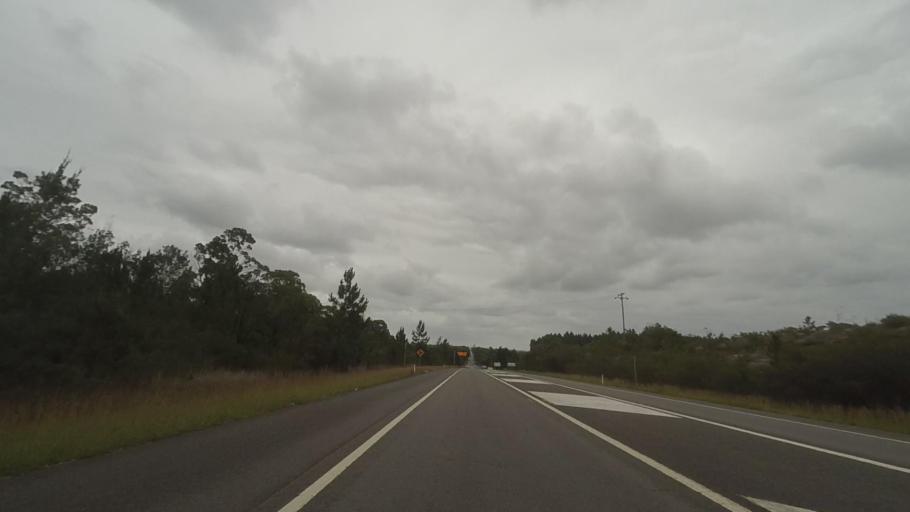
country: AU
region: New South Wales
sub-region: Wyong Shire
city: Charmhaven
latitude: -33.2062
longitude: 151.4971
